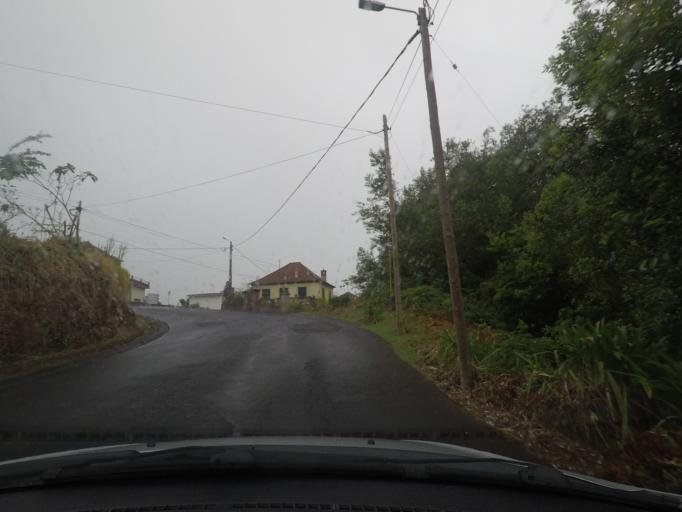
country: PT
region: Madeira
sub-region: Santana
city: Santana
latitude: 32.7951
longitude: -16.8709
